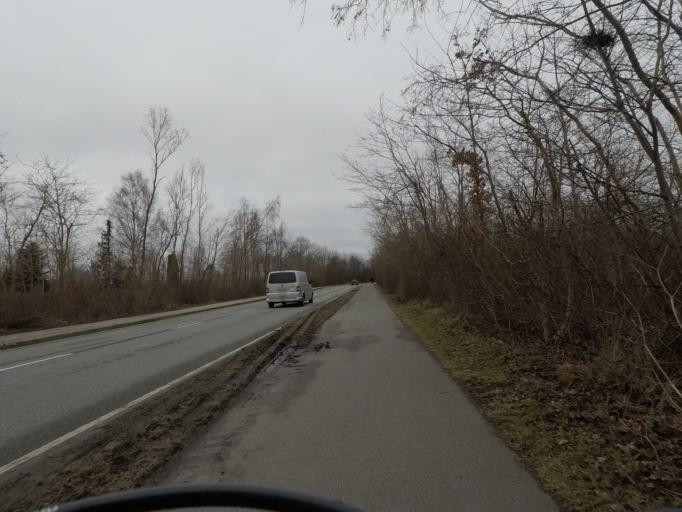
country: DK
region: Capital Region
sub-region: Egedal Kommune
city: Smorumnedre
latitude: 55.7198
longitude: 12.3256
